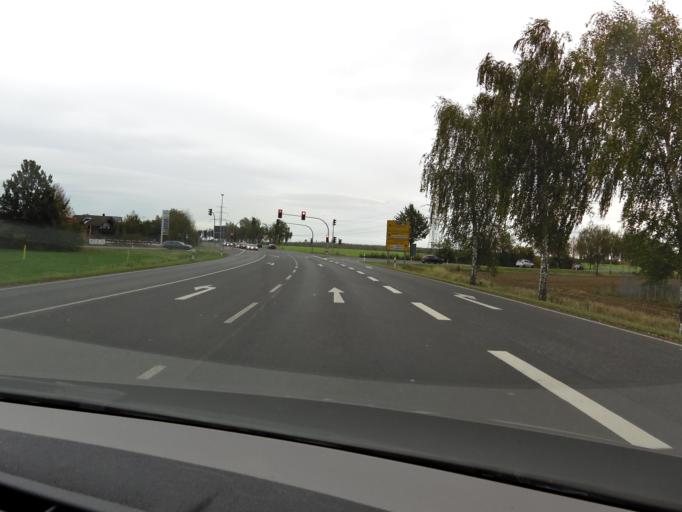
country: DE
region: Saxony
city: Zwenkau
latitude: 51.2042
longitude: 12.3298
